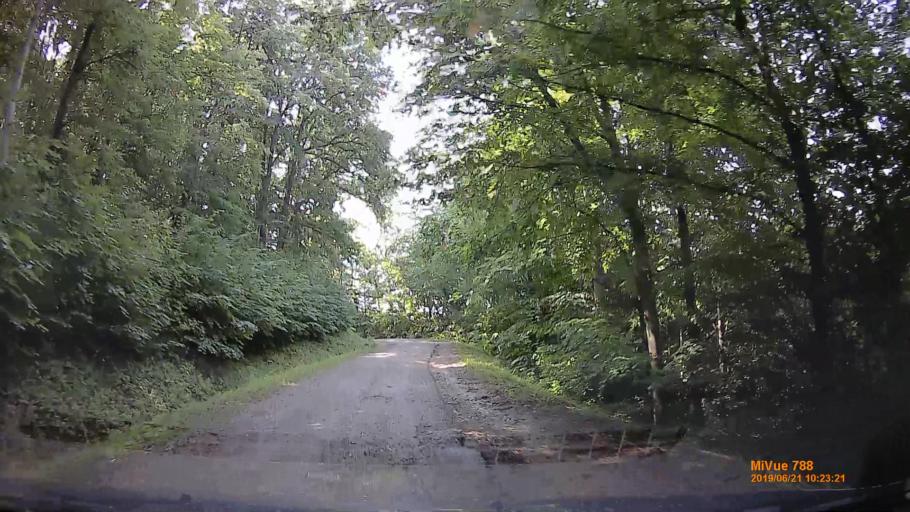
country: HU
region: Baranya
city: Buekkoesd
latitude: 46.1866
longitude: 17.9701
